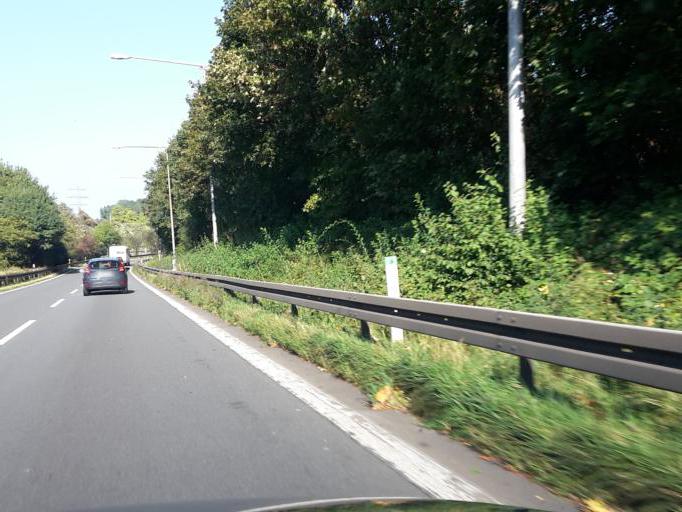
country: DE
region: North Rhine-Westphalia
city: Opladen
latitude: 51.0410
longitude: 7.0093
